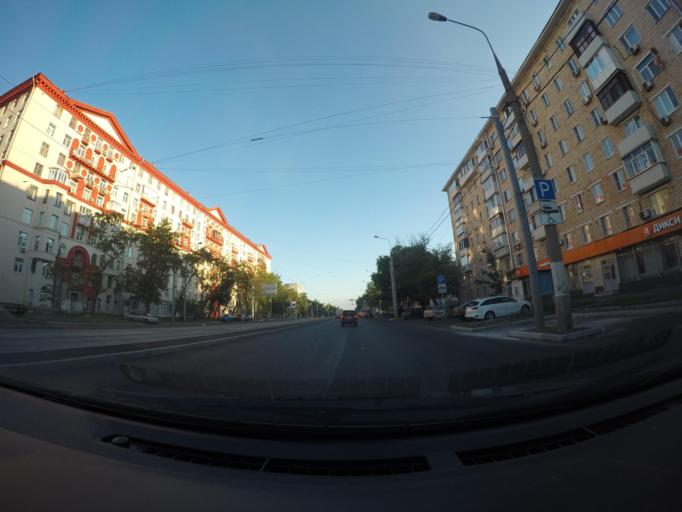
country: RU
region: Moscow
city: Lefortovo
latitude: 55.7618
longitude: 37.7360
